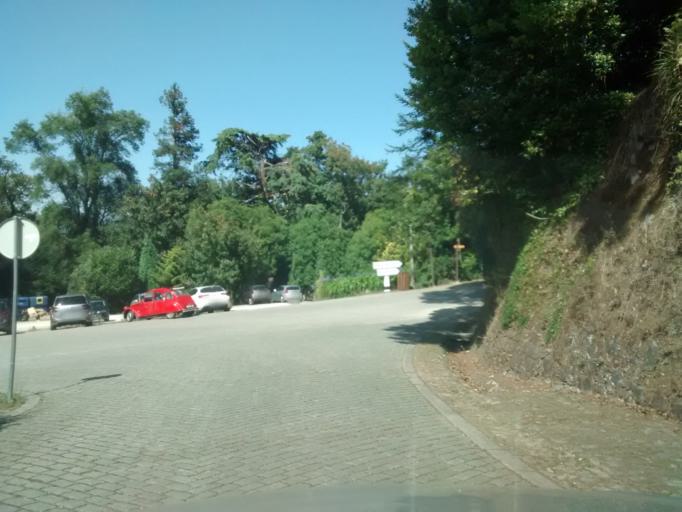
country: PT
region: Aveiro
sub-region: Mealhada
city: Pampilhosa do Botao
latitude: 40.3759
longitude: -8.3642
